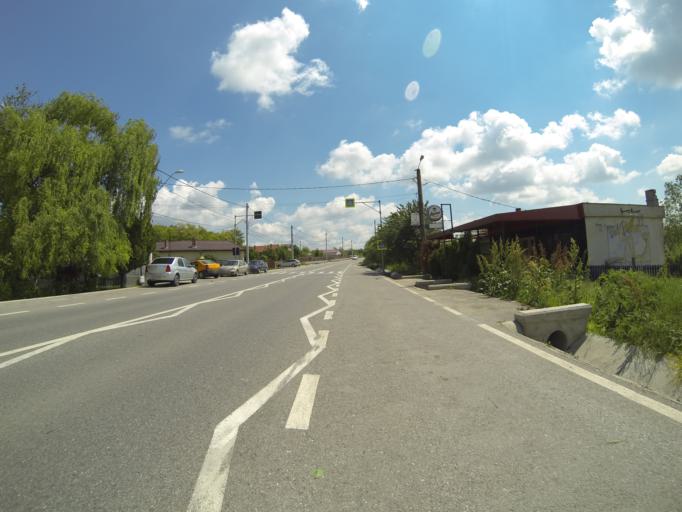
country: RO
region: Dolj
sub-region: Comuna Carcea
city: Carcea
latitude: 44.2688
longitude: 23.8833
